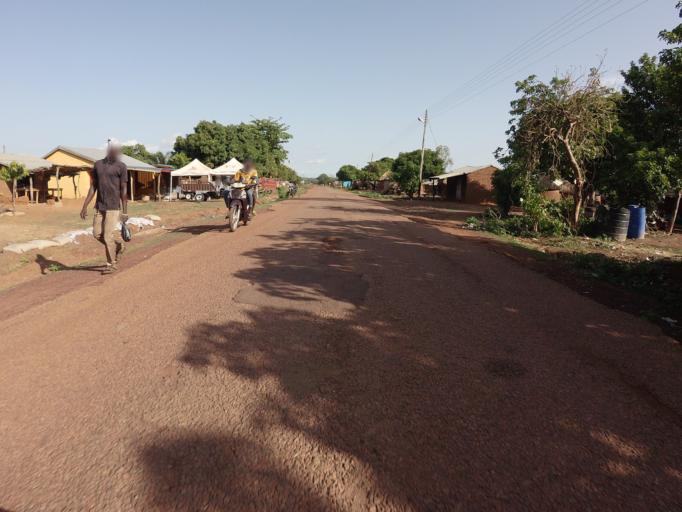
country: GH
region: Upper East
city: Bawku
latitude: 10.6295
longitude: -0.1802
